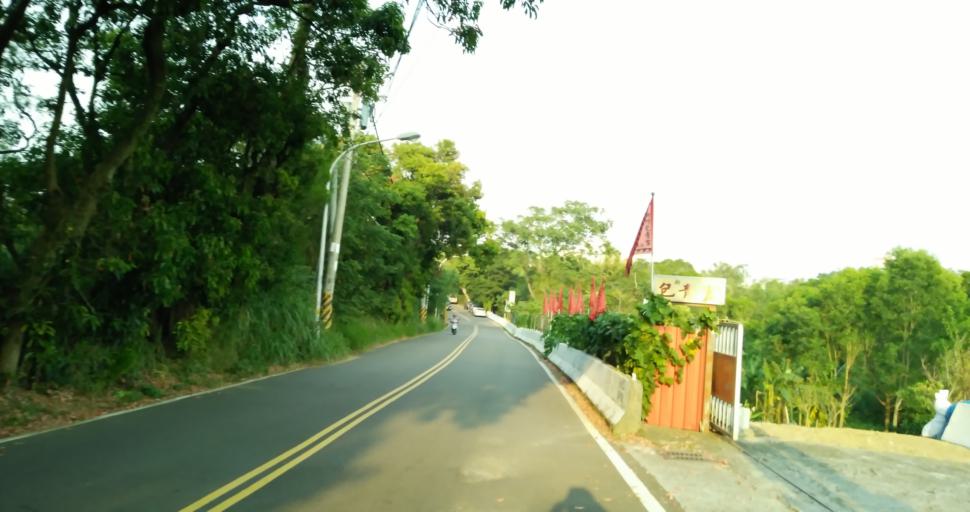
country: TW
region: Taiwan
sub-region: Hsinchu
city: Hsinchu
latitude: 24.7768
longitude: 120.9771
